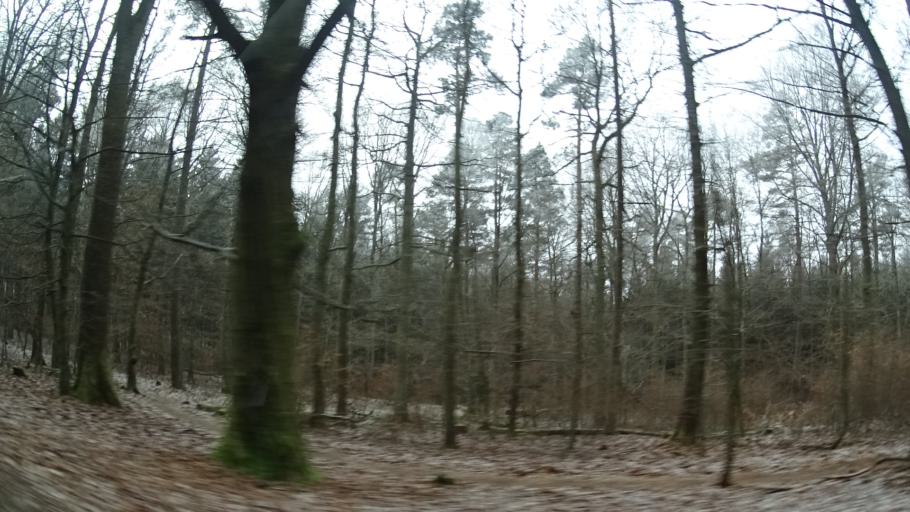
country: DE
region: Hesse
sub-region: Regierungsbezirk Darmstadt
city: Bad Orb
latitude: 50.1856
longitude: 9.4233
